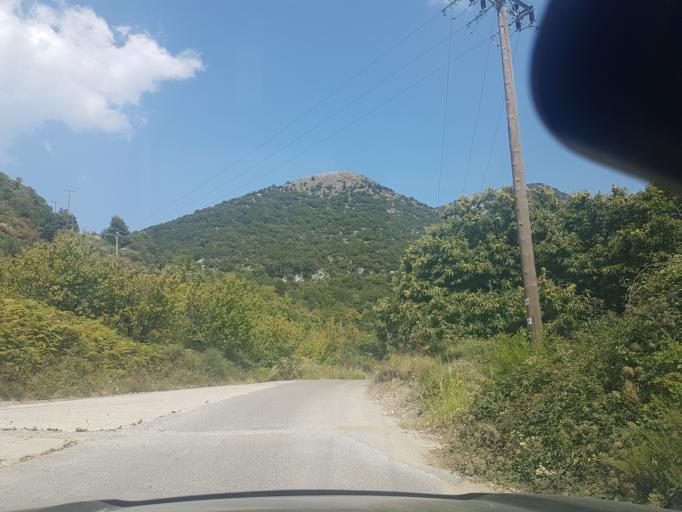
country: GR
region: Central Greece
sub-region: Nomos Evvoias
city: Kymi
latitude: 38.6451
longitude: 23.8999
